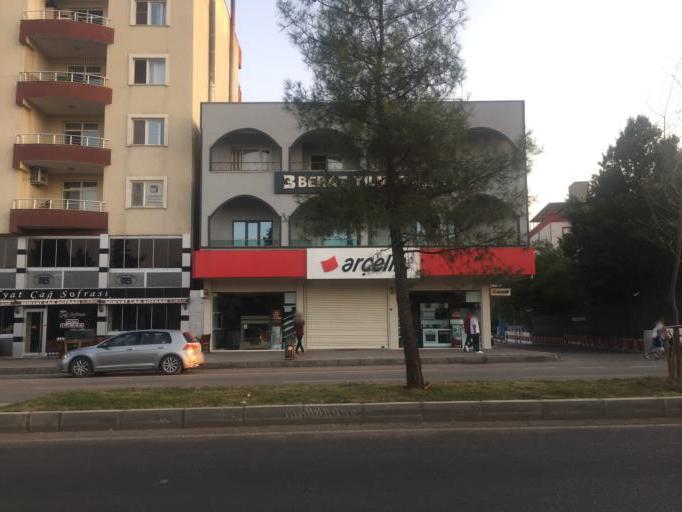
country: TR
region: Mardin
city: Midyat
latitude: 37.4244
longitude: 41.3407
